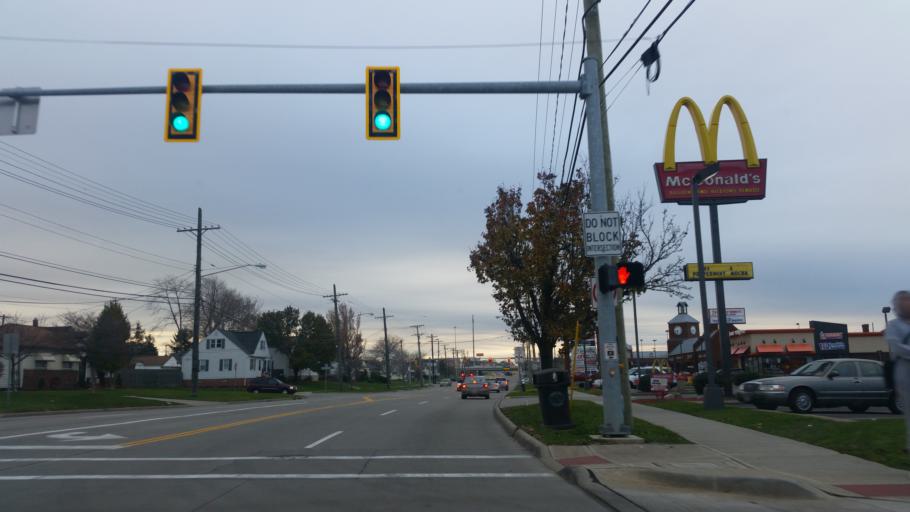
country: US
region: Ohio
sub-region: Cuyahoga County
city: Brooklyn
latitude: 41.4267
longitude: -81.7345
